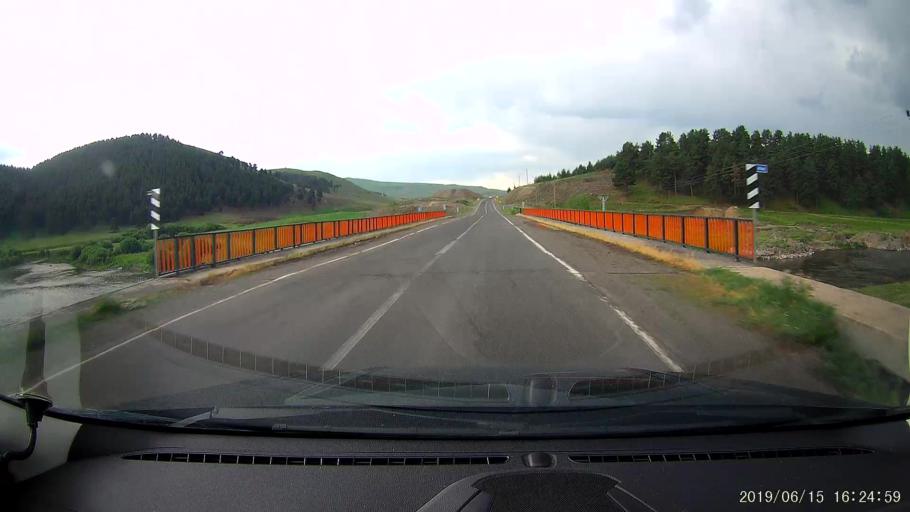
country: TR
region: Ardahan
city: Hanak
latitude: 41.1600
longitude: 42.8719
